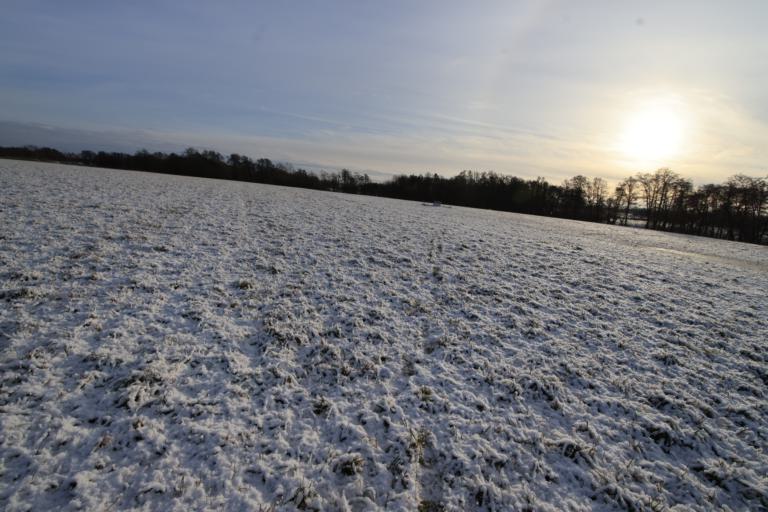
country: SE
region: Halland
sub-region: Varbergs Kommun
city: Varberg
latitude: 57.1321
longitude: 12.2818
